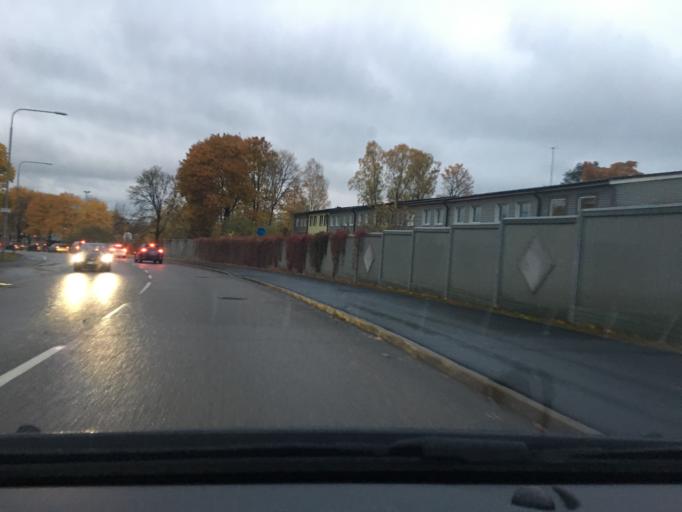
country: SE
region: Stockholm
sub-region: Stockholms Kommun
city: Kista
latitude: 59.3747
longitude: 17.9036
